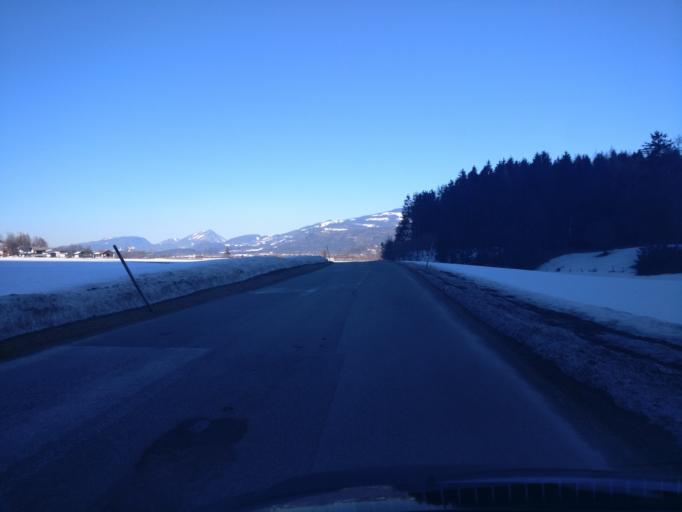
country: AT
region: Salzburg
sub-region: Politischer Bezirk Hallein
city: Kuchl
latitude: 47.6050
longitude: 13.1426
